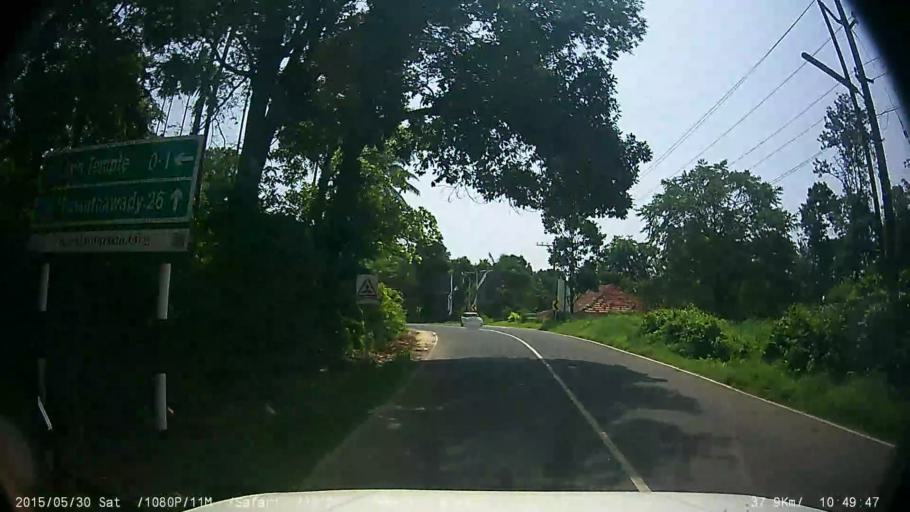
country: IN
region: Kerala
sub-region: Wayanad
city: Kalpetta
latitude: 11.6394
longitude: 76.0864
